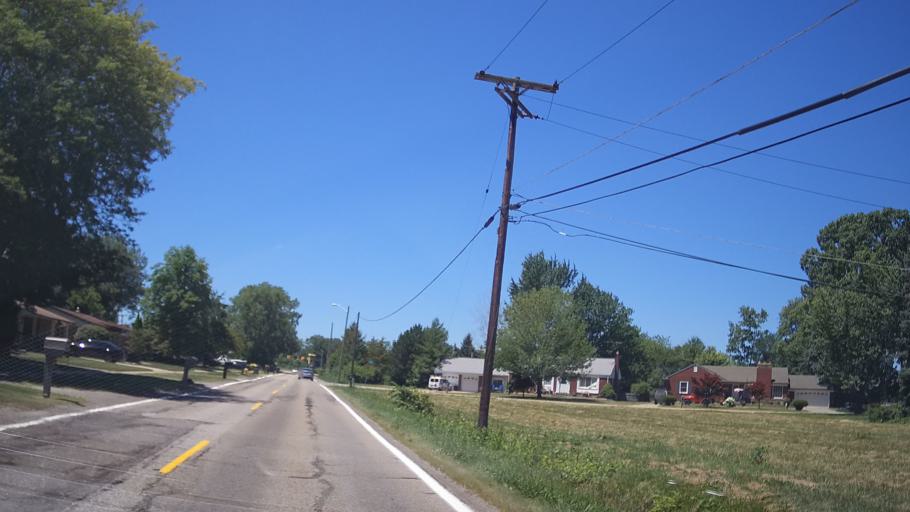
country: US
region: Michigan
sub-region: Macomb County
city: Clinton
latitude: 42.5637
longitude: -82.9128
